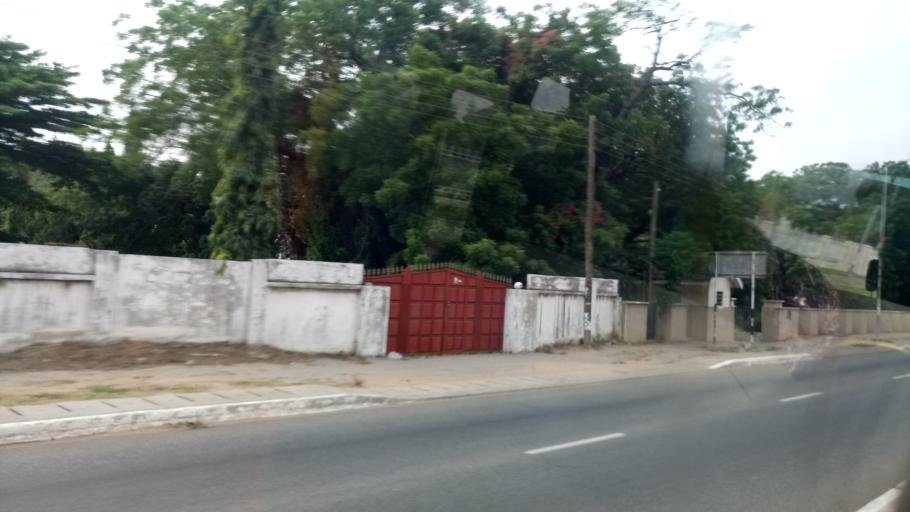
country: GH
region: Greater Accra
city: Accra
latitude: 5.5675
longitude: -0.1929
